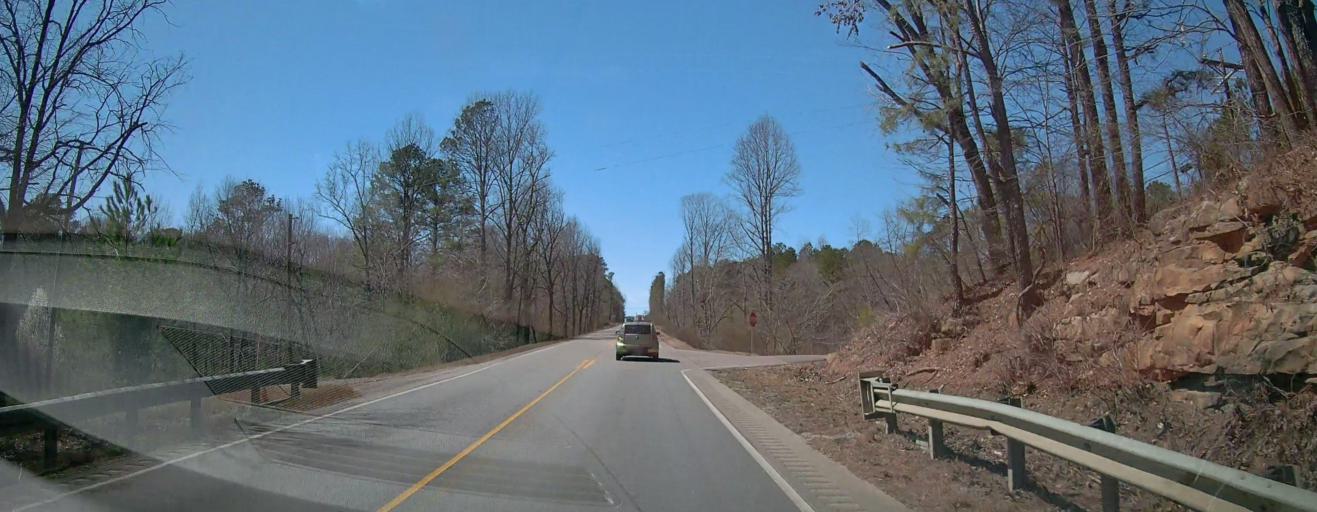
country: US
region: Alabama
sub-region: Cullman County
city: Hanceville
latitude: 34.1724
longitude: -86.6958
